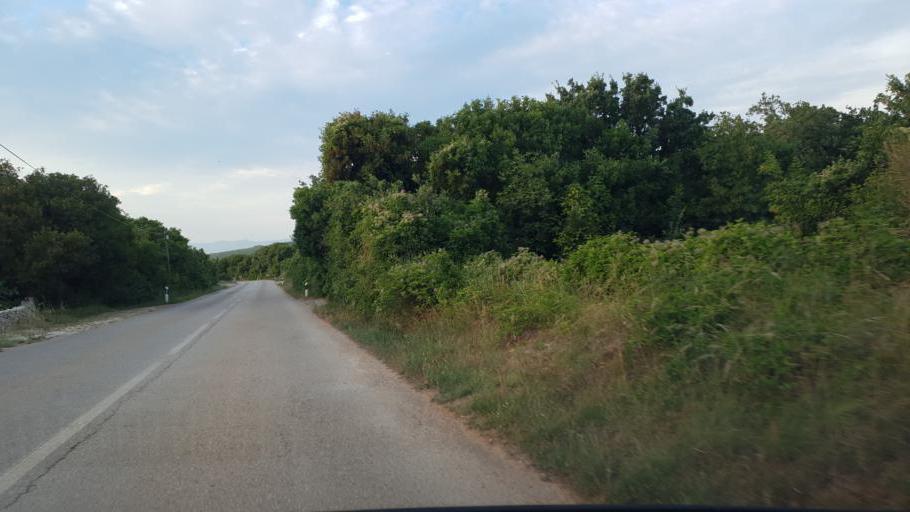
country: HR
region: Primorsko-Goranska
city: Punat
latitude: 45.0031
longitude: 14.6336
